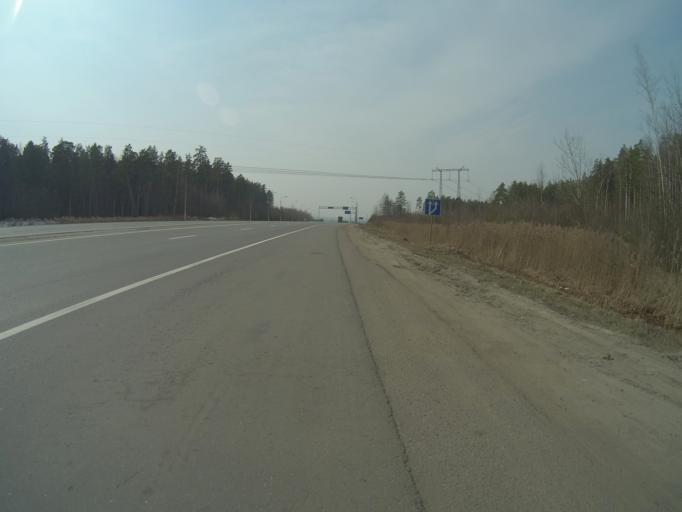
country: RU
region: Vladimir
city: Kommunar
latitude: 56.0594
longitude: 40.4487
